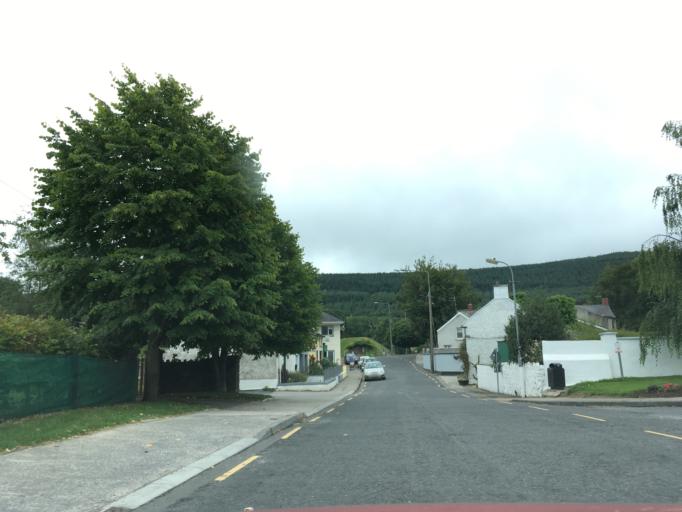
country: IE
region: Munster
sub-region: South Tipperary
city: Cluain Meala
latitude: 52.3625
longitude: -7.5806
